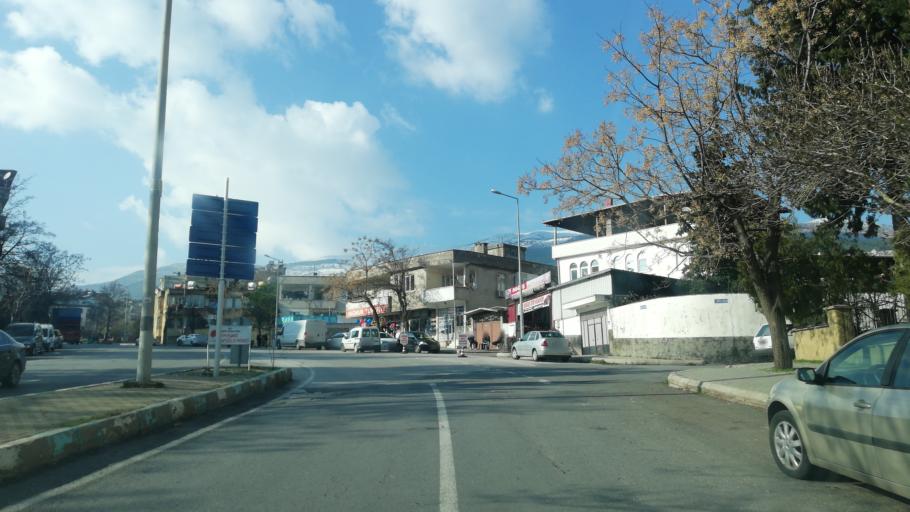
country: TR
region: Kahramanmaras
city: Kahramanmaras
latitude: 37.5885
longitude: 36.9086
